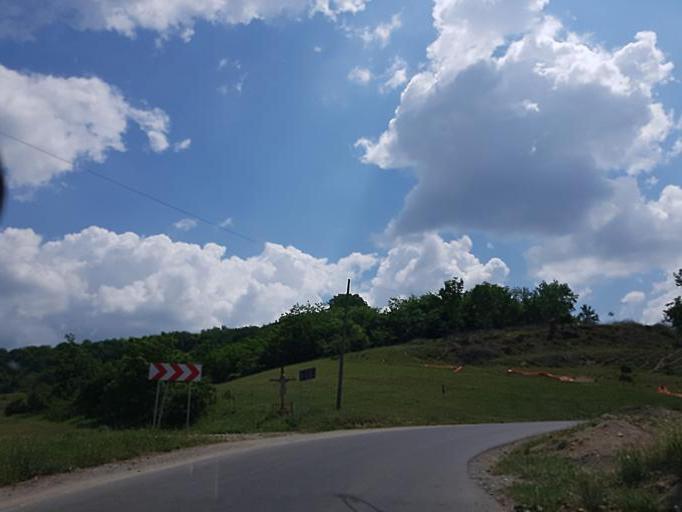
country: RO
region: Sibiu
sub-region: Comuna Seica Mica
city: Seica Mica
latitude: 46.0513
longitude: 24.1455
